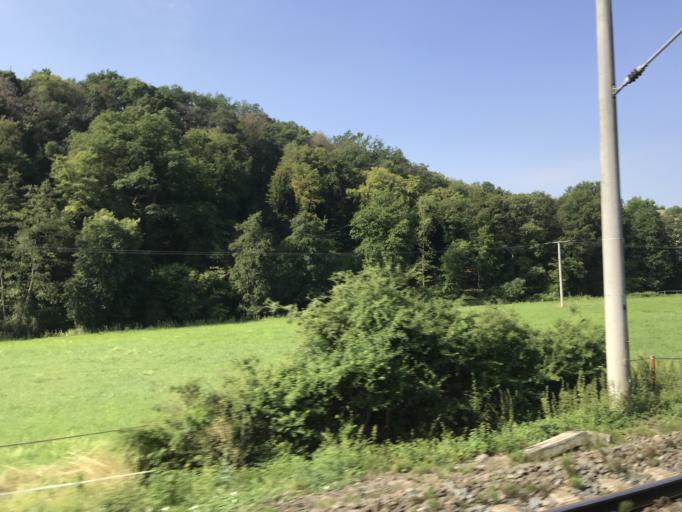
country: DE
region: Hesse
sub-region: Regierungsbezirk Giessen
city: Villmar
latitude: 50.3483
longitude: 8.1990
